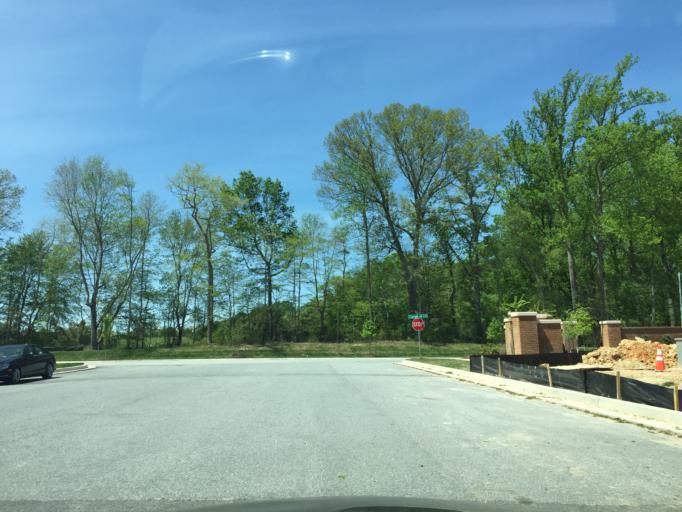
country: US
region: Maryland
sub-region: Baltimore County
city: White Marsh
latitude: 39.3575
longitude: -76.4168
